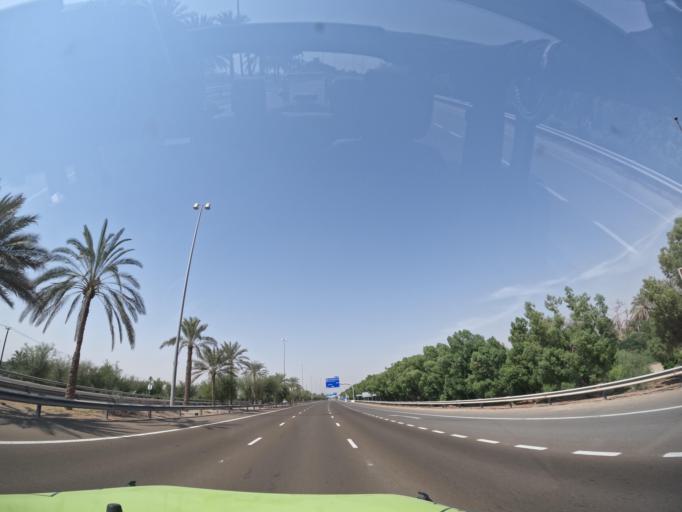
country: AE
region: Abu Dhabi
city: Al Ain
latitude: 24.1849
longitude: 55.3390
